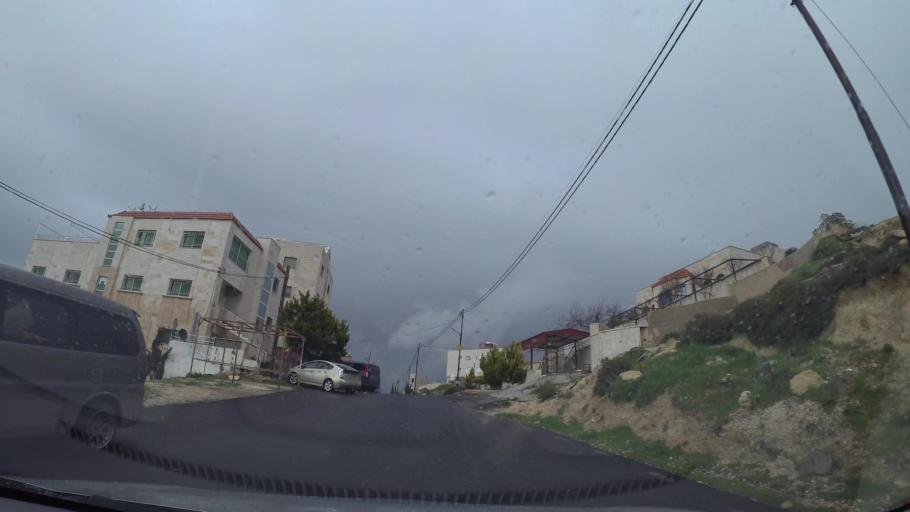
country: JO
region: Amman
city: Al Jubayhah
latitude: 32.0350
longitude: 35.8429
